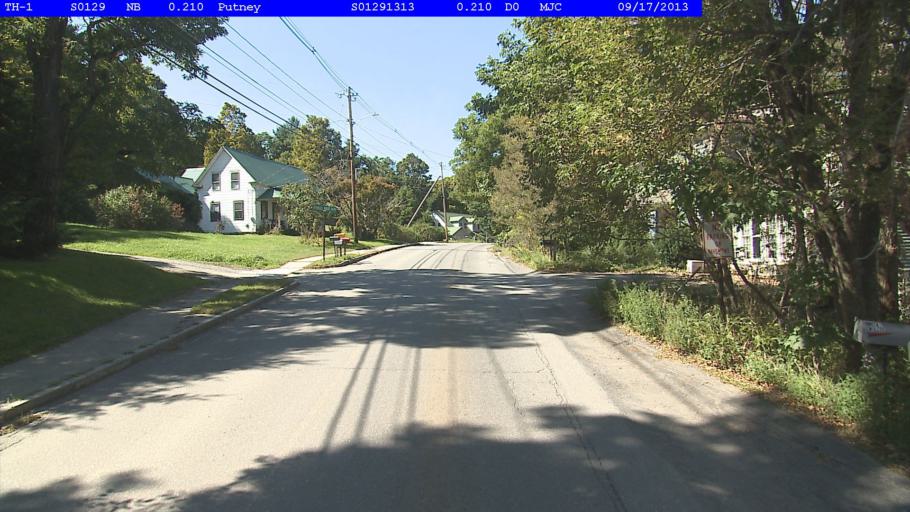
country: US
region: New Hampshire
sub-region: Cheshire County
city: Westmoreland
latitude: 42.9767
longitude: -72.5251
